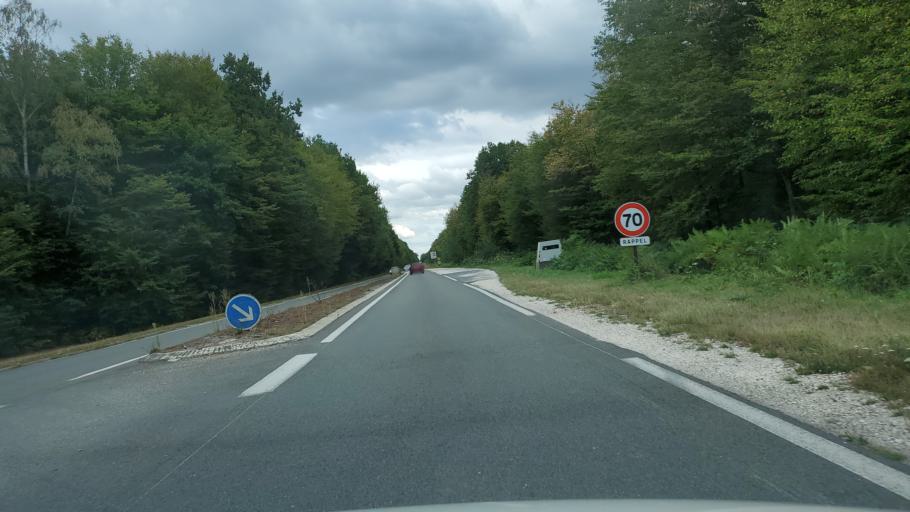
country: FR
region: Ile-de-France
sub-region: Departement de Seine-et-Marne
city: Mortcerf
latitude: 48.7756
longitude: 2.8998
